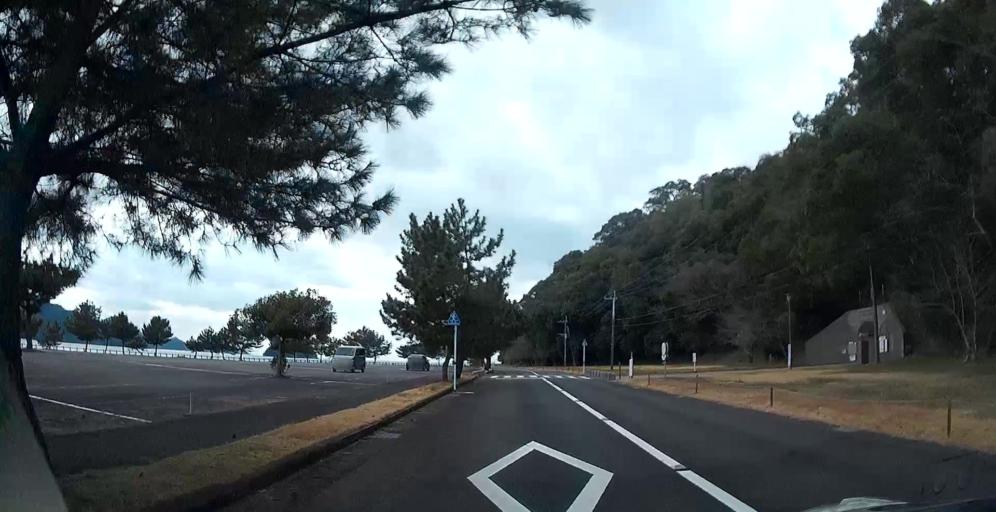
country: JP
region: Kumamoto
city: Minamata
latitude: 32.3614
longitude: 130.4898
